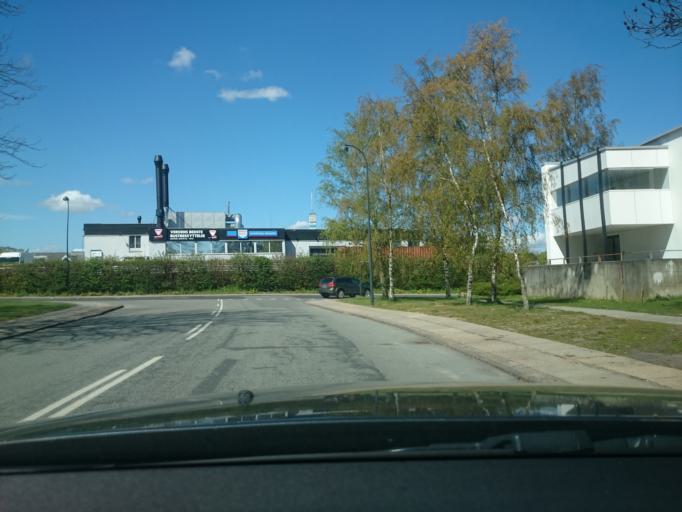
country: DK
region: Capital Region
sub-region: Lyngby-Tarbaek Kommune
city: Kongens Lyngby
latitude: 55.7541
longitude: 12.5136
